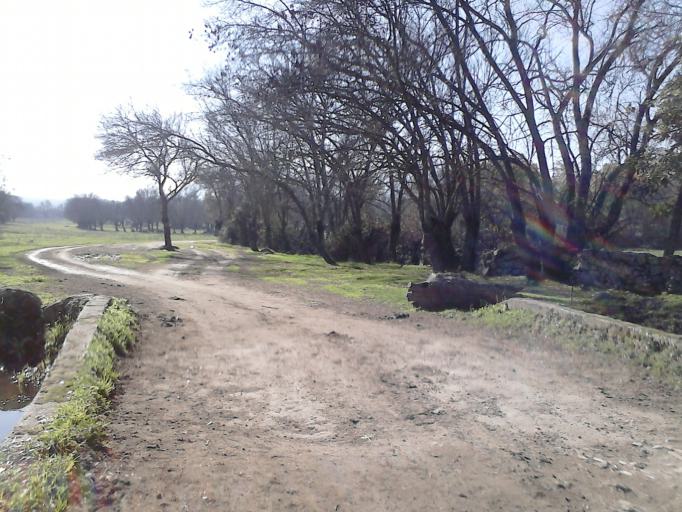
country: ES
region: Madrid
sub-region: Provincia de Madrid
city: El Escorial
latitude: 40.5914
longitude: -4.1138
